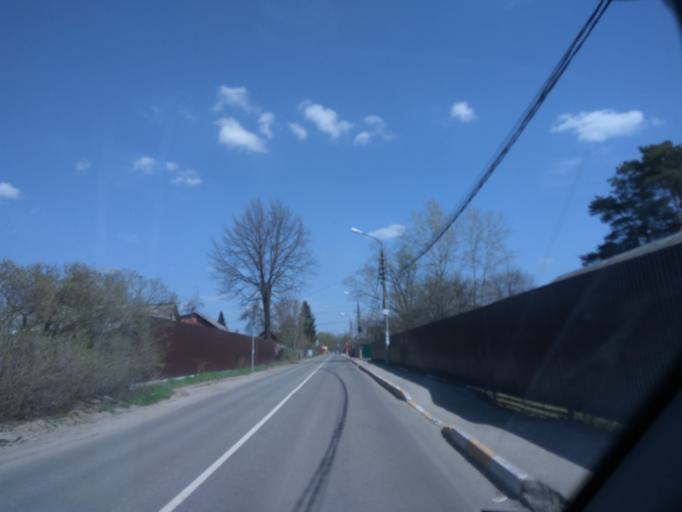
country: RU
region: Moskovskaya
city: Ramenskoye
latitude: 55.5605
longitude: 38.2155
